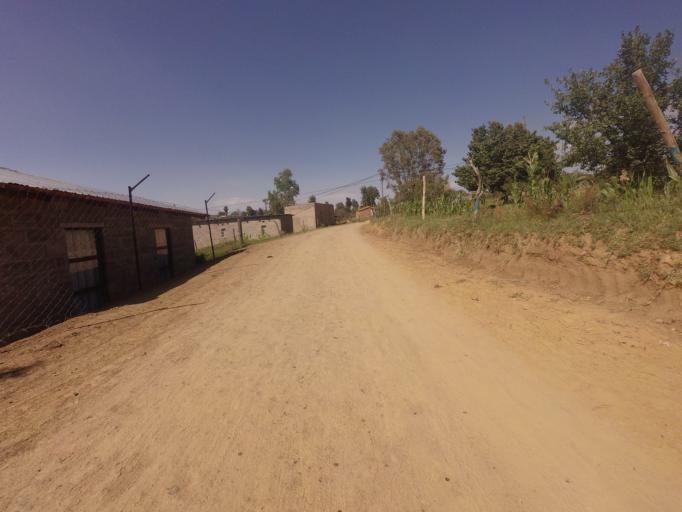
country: LS
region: Berea
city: Teyateyaneng
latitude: -29.1440
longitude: 27.7535
